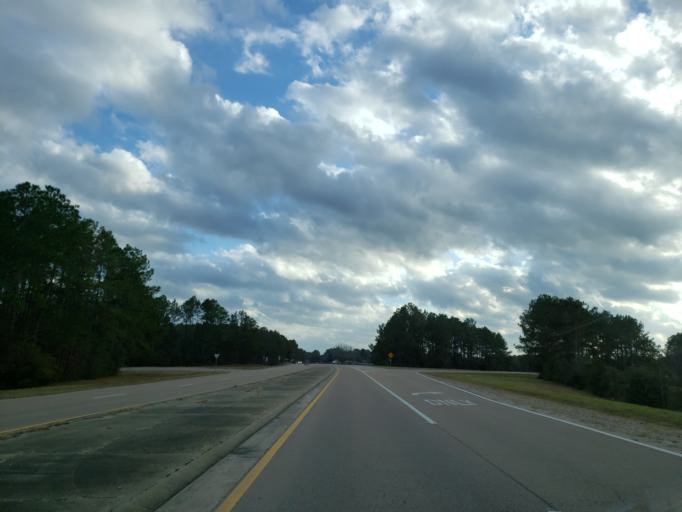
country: US
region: Mississippi
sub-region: Forrest County
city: Hattiesburg
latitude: 31.2424
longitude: -89.3017
